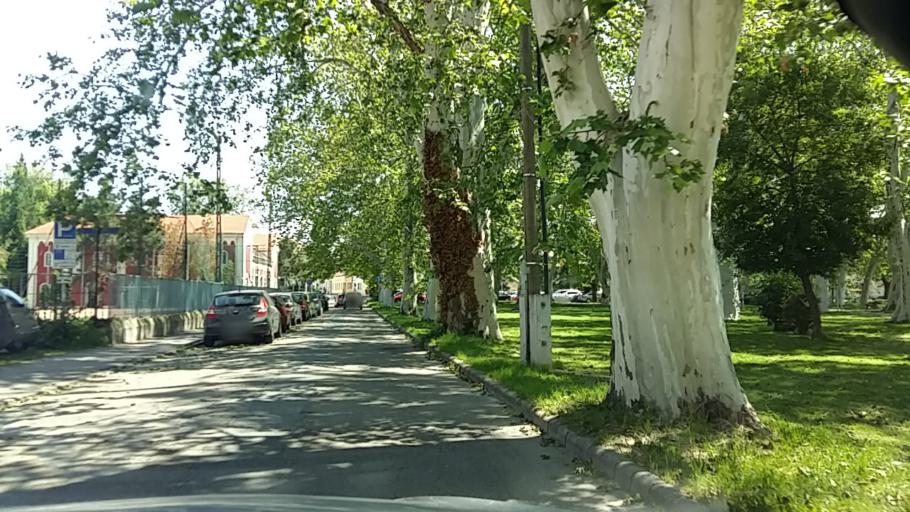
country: HU
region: Gyor-Moson-Sopron
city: Sopron
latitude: 47.6830
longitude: 16.5947
